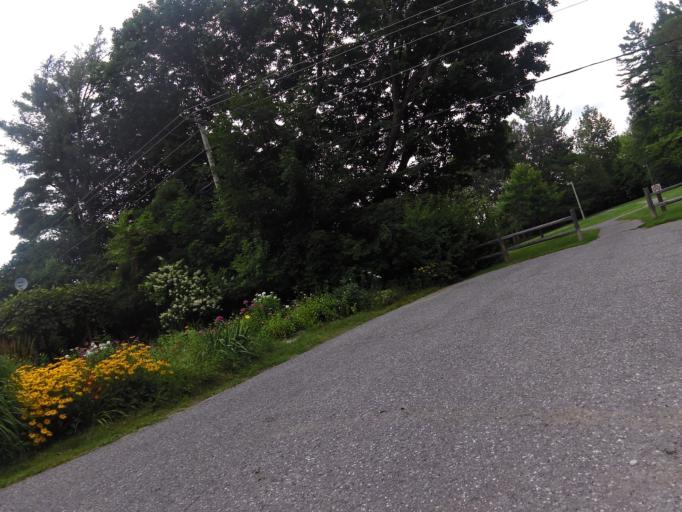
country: CA
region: Ontario
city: Bells Corners
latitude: 45.3261
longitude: -75.8131
